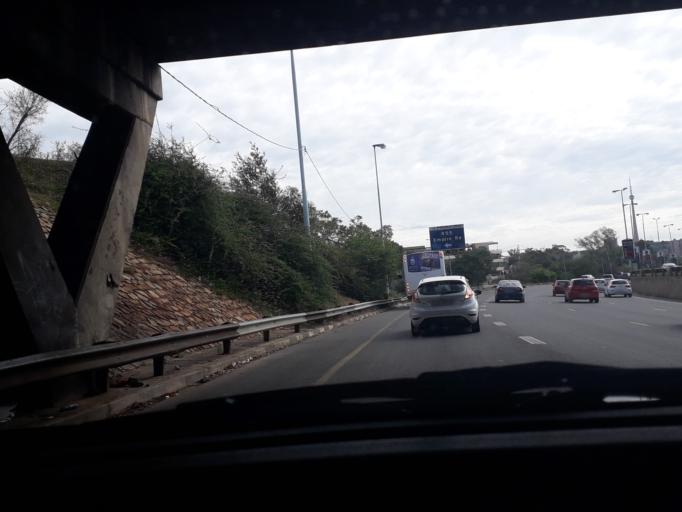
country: ZA
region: Gauteng
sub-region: City of Johannesburg Metropolitan Municipality
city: Johannesburg
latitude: -26.1839
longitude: 28.0324
